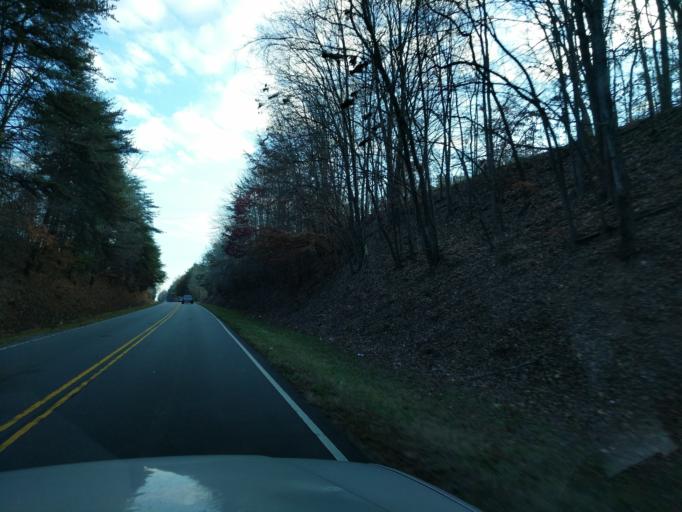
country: US
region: North Carolina
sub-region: Rutherford County
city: Rutherfordton
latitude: 35.4268
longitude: -81.9804
